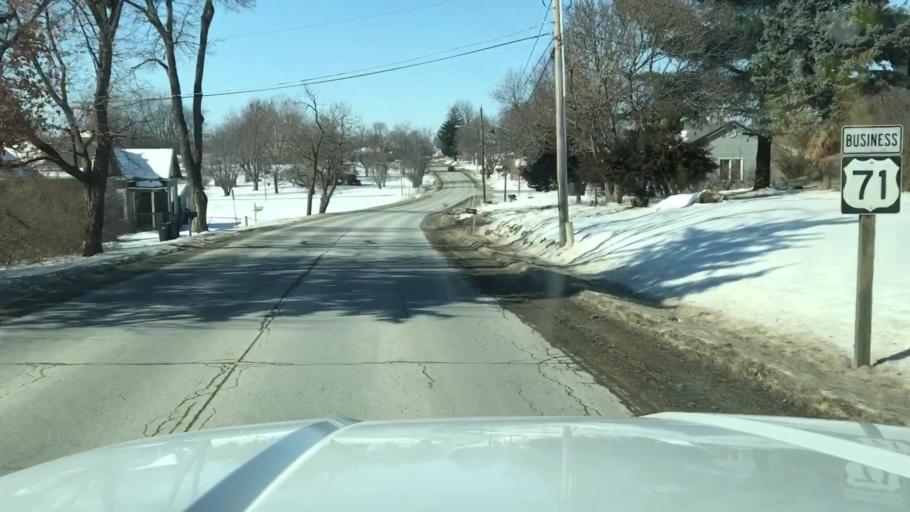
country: US
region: Missouri
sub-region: Andrew County
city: Savannah
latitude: 39.9468
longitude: -94.8319
